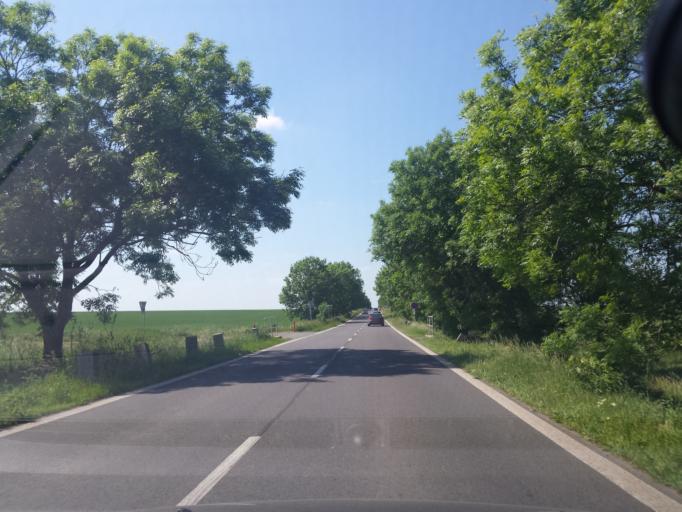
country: CZ
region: Central Bohemia
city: Horomerice
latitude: 50.1230
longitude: 14.3526
